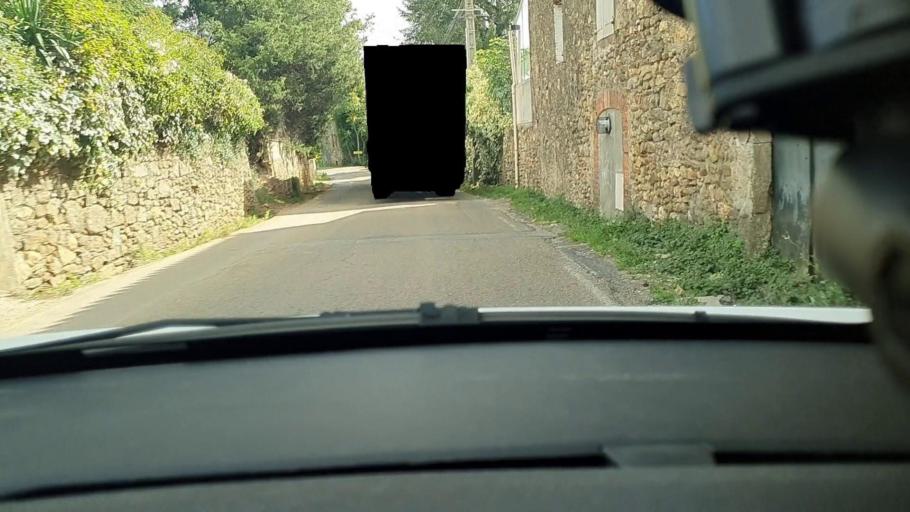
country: FR
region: Languedoc-Roussillon
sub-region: Departement du Gard
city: Saint-Florent-sur-Auzonnet
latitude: 44.2404
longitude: 4.1074
